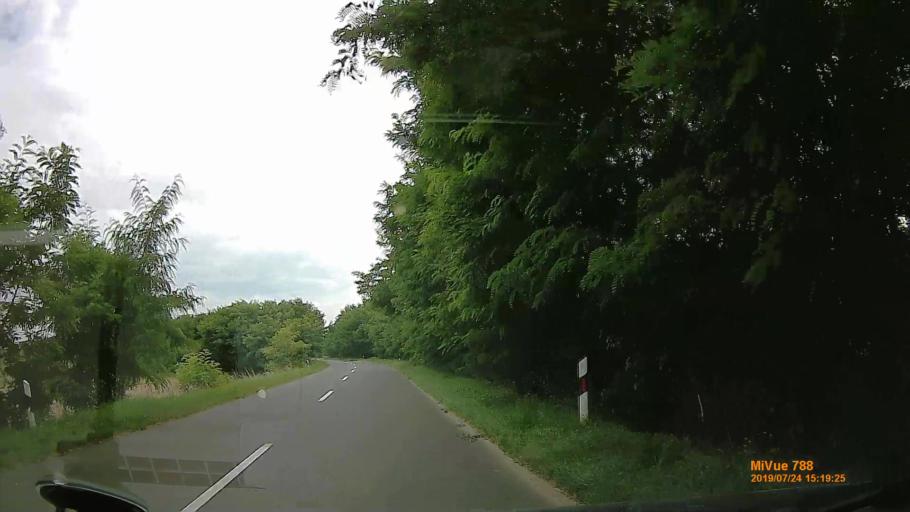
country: HU
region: Szabolcs-Szatmar-Bereg
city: Tarpa
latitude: 48.1700
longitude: 22.5435
